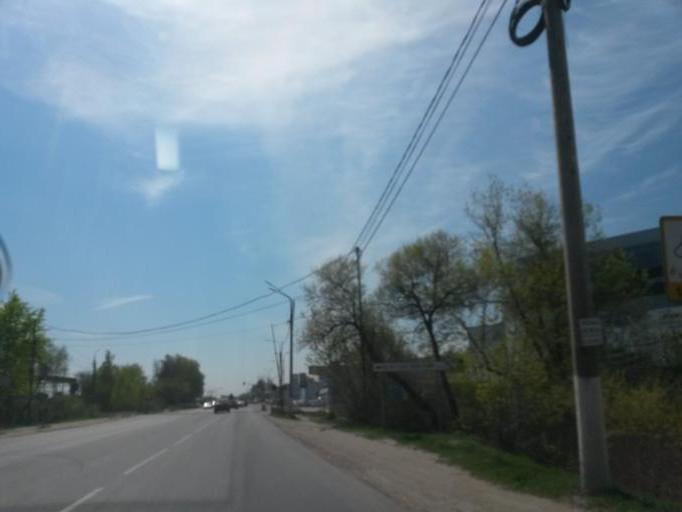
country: RU
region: Moskovskaya
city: Shcherbinka
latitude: 55.4692
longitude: 37.5616
